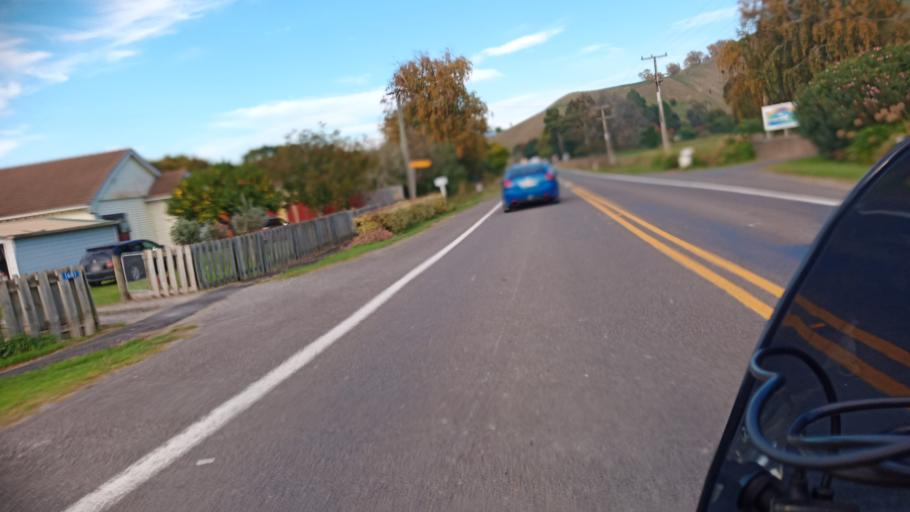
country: NZ
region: Gisborne
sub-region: Gisborne District
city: Gisborne
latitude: -38.7562
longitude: 177.9213
